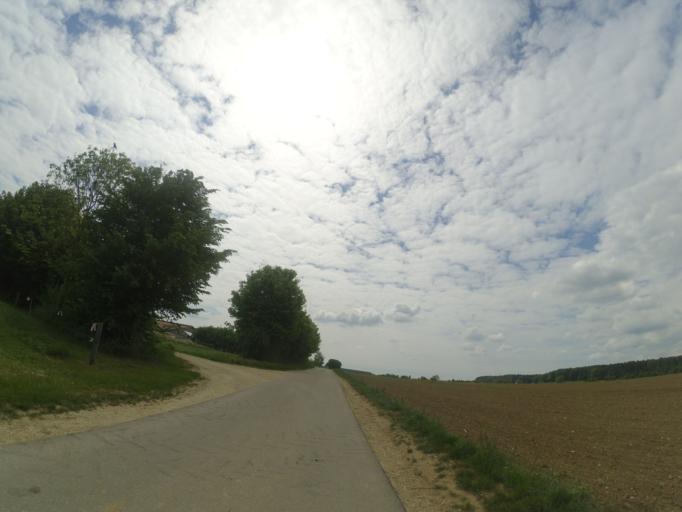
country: DE
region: Baden-Wuerttemberg
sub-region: Tuebingen Region
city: Berghulen
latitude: 48.4517
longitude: 9.7708
